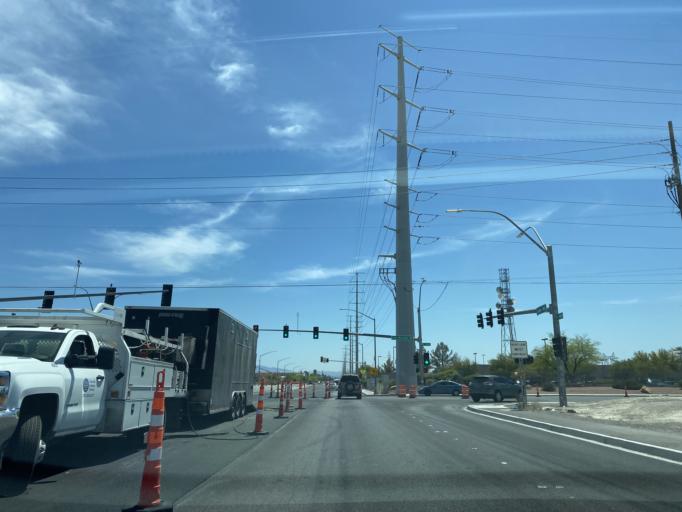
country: US
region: Nevada
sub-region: Clark County
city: North Las Vegas
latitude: 36.2475
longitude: -115.1170
